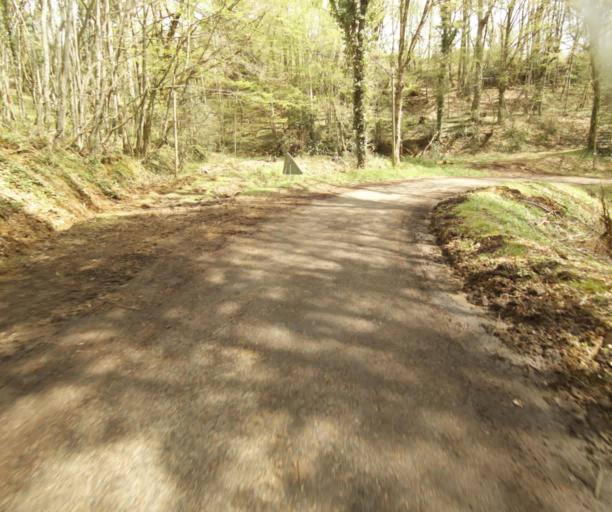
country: FR
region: Limousin
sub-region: Departement de la Correze
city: Tulle
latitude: 45.2829
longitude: 1.7995
